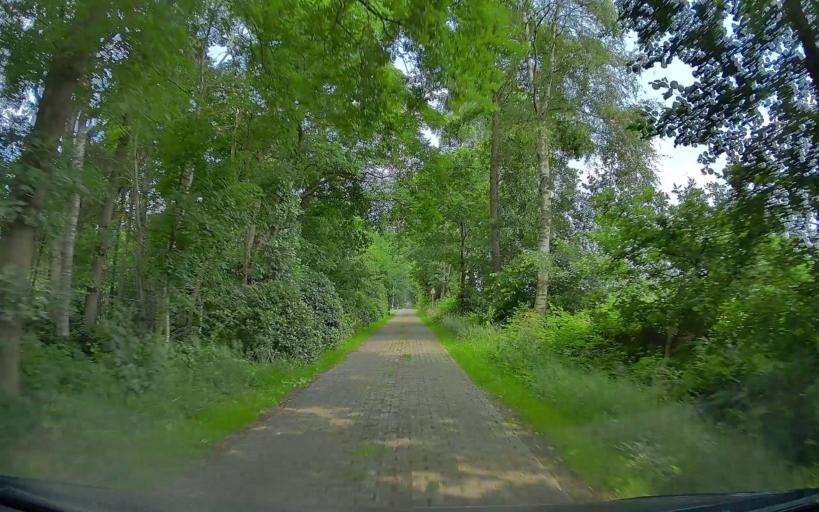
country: DE
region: Lower Saxony
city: Bosel
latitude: 52.9955
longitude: 7.9008
